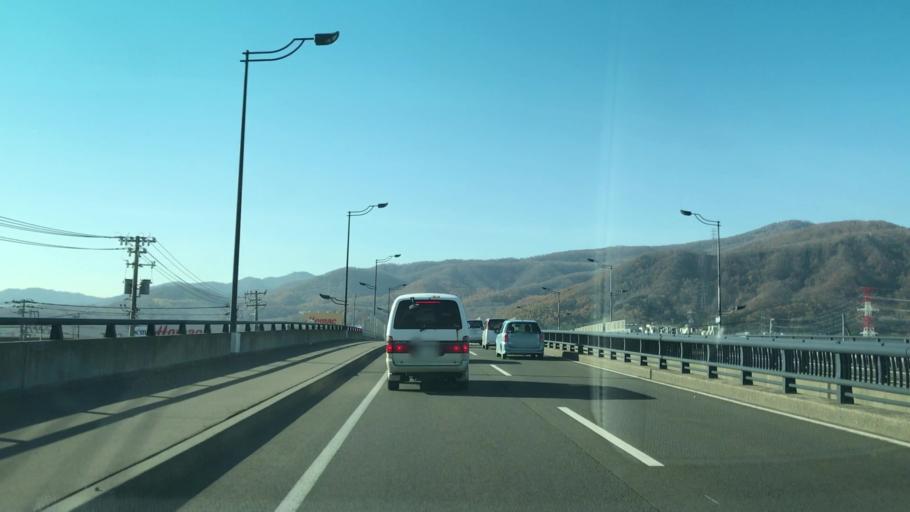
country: JP
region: Hokkaido
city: Sapporo
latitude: 43.1041
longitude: 141.2724
